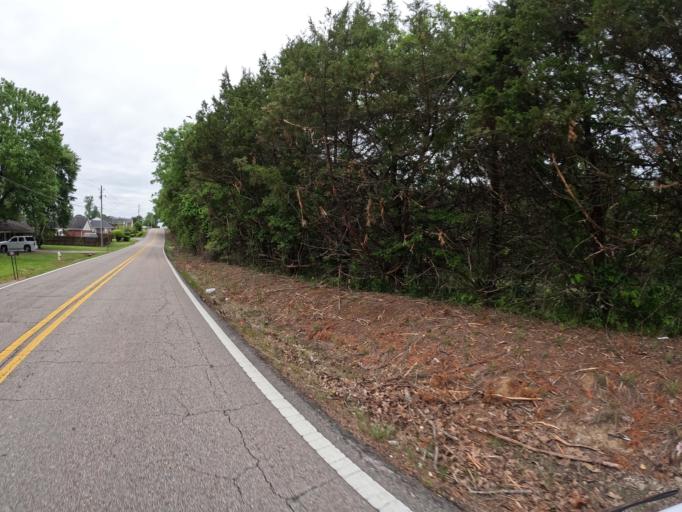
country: US
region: Mississippi
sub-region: Lee County
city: Tupelo
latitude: 34.2850
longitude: -88.7653
